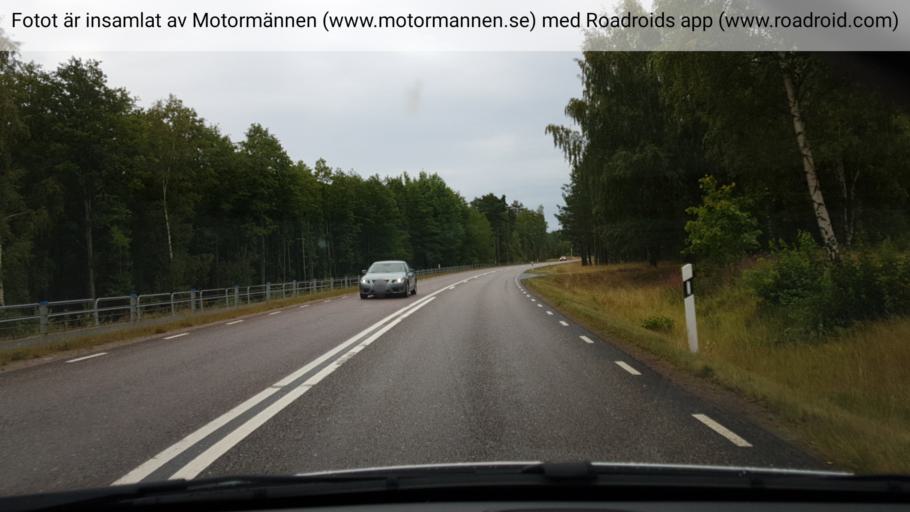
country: SE
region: Vaestra Goetaland
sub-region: Karlsborgs Kommun
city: Karlsborg
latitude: 58.5107
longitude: 14.4678
